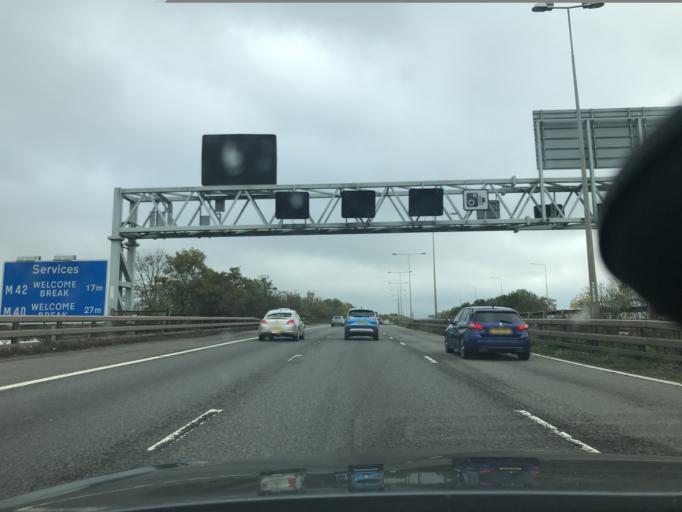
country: GB
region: England
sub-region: Solihull
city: Chelmsley Wood
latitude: 52.4821
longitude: -1.7102
